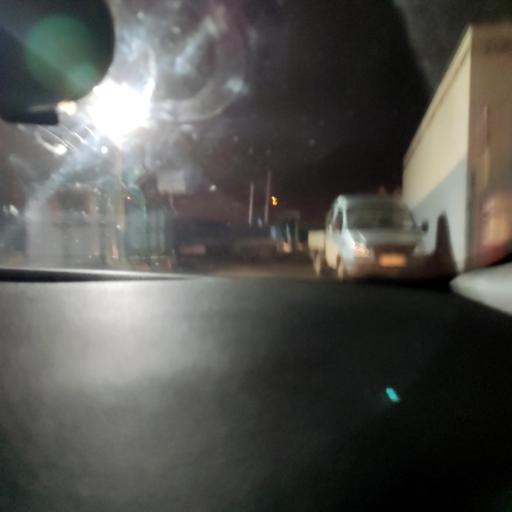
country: RU
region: Moskovskaya
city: Shcherbinka
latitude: 55.5250
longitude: 37.5220
